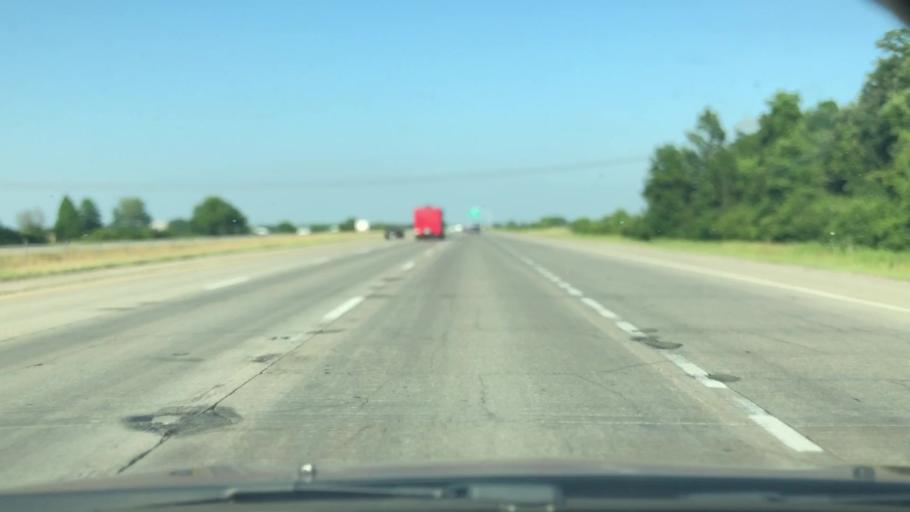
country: US
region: Ohio
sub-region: Madison County
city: West Jefferson
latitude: 39.9563
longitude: -83.3689
